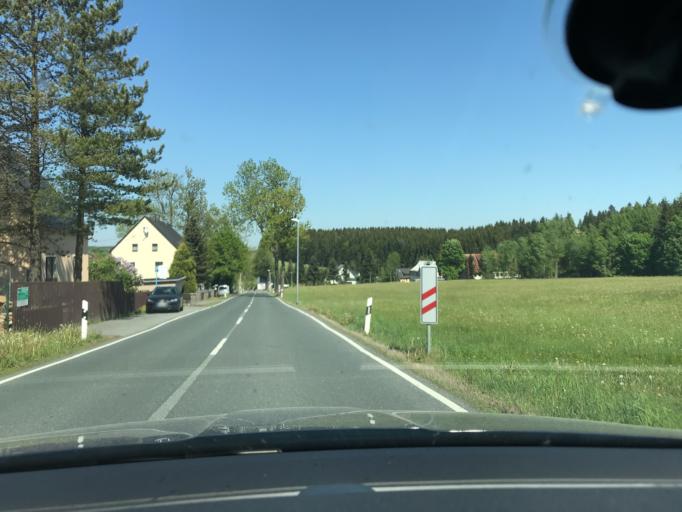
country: CZ
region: Ustecky
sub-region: Okres Chomutov
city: Vejprty
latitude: 50.4660
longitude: 12.9903
